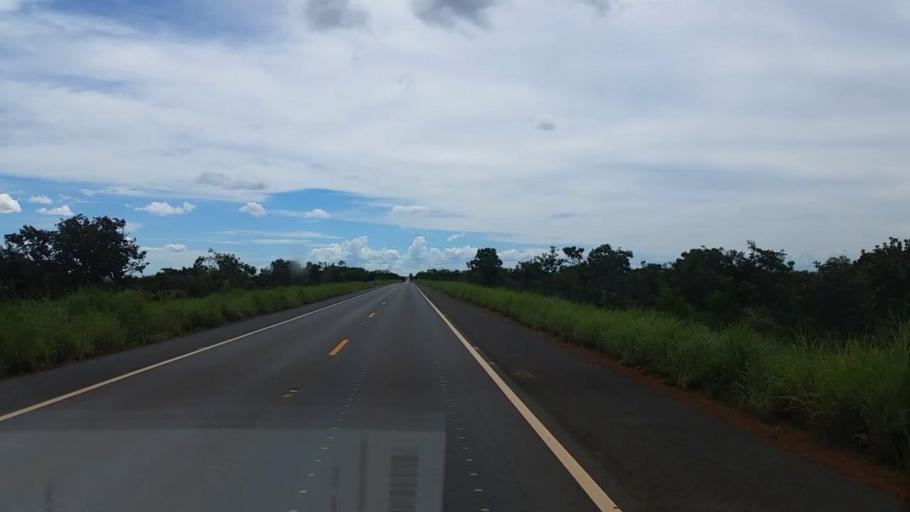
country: BR
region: Goias
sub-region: Luziania
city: Luziania
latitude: -16.2082
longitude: -47.4240
